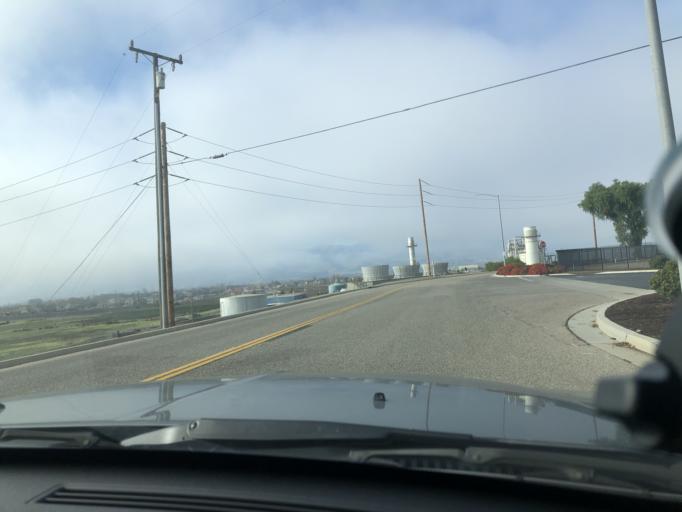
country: US
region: California
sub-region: Monterey County
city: King City
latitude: 36.2260
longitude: -121.1253
